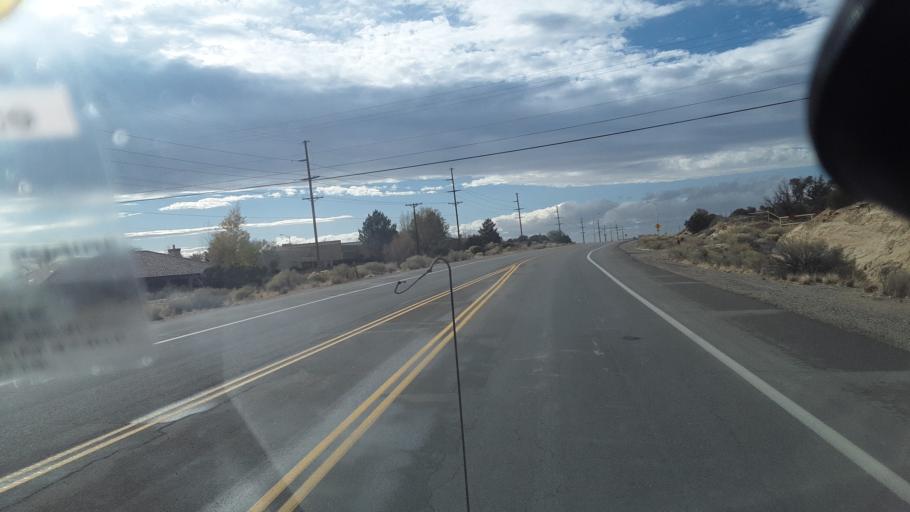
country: US
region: New Mexico
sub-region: San Juan County
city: Farmington
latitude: 36.7738
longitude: -108.1882
